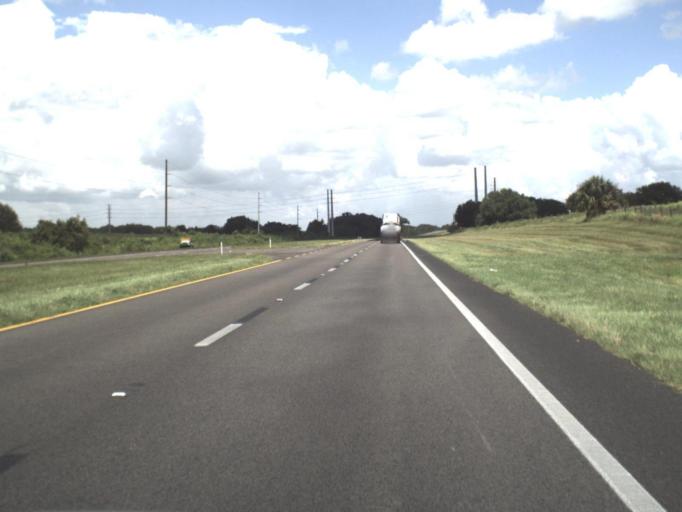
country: US
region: Florida
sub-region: Polk County
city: Fort Meade
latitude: 27.8055
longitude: -81.8188
